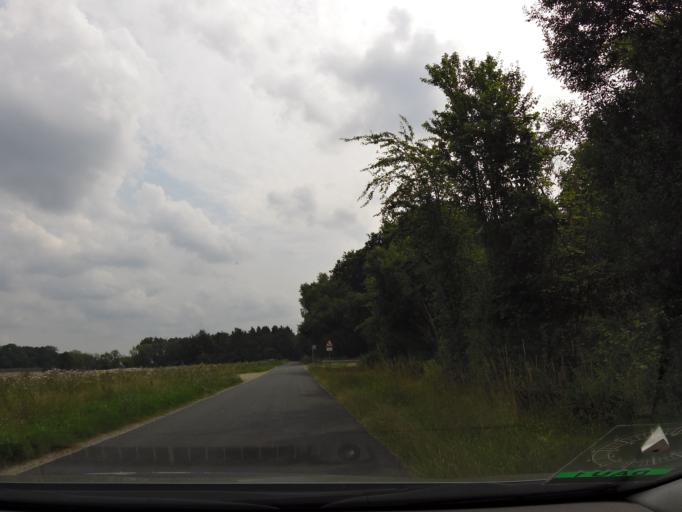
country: DK
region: South Denmark
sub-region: Odense Kommune
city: Neder Holluf
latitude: 55.3817
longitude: 10.4743
